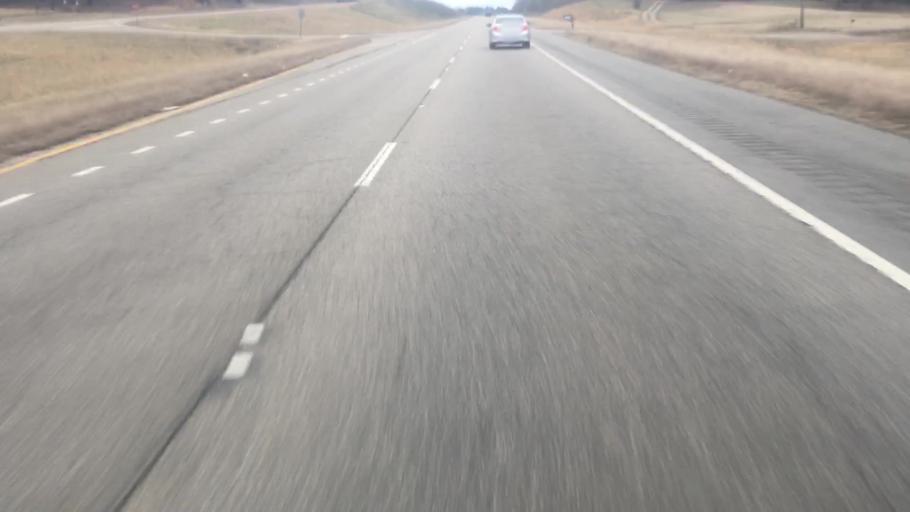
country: US
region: Alabama
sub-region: Walker County
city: Cordova
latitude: 33.8039
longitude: -87.1278
